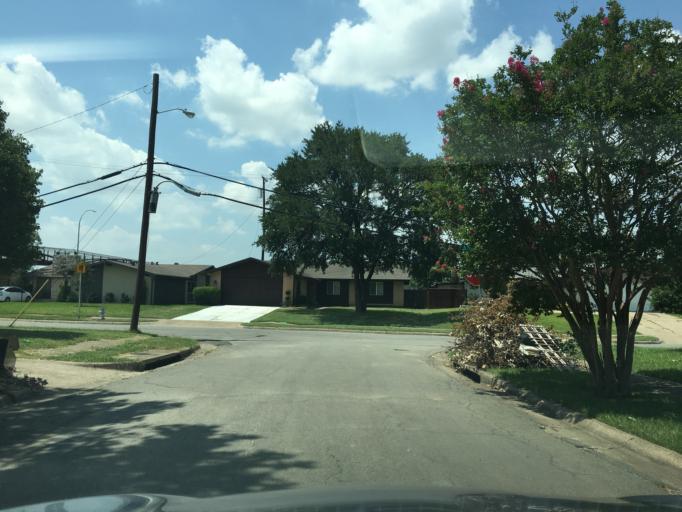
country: US
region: Texas
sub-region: Dallas County
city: Farmers Branch
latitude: 32.9141
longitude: -96.8630
